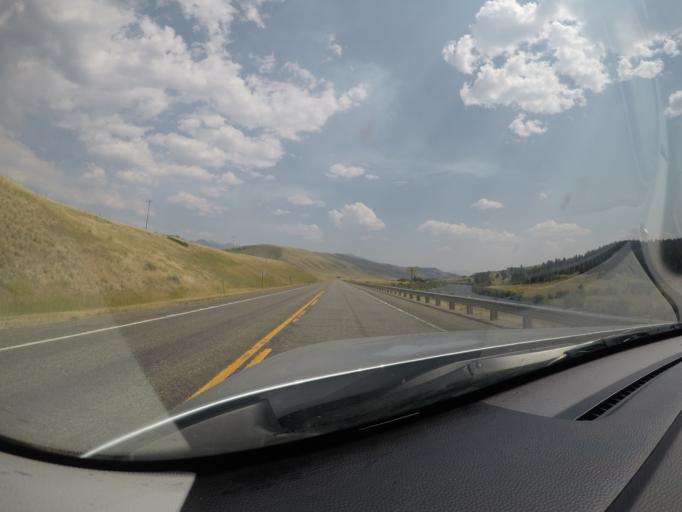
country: US
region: Montana
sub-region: Gallatin County
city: Big Sky
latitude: 44.9663
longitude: -111.6378
